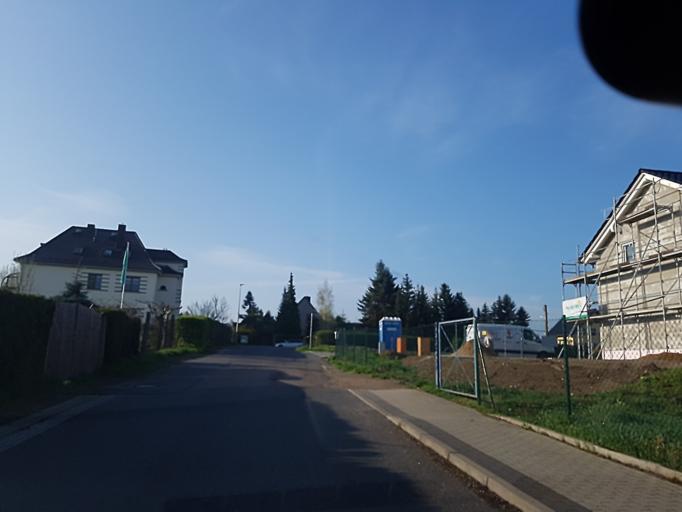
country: DE
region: Saxony
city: Oschatz
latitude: 51.2955
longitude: 13.0995
